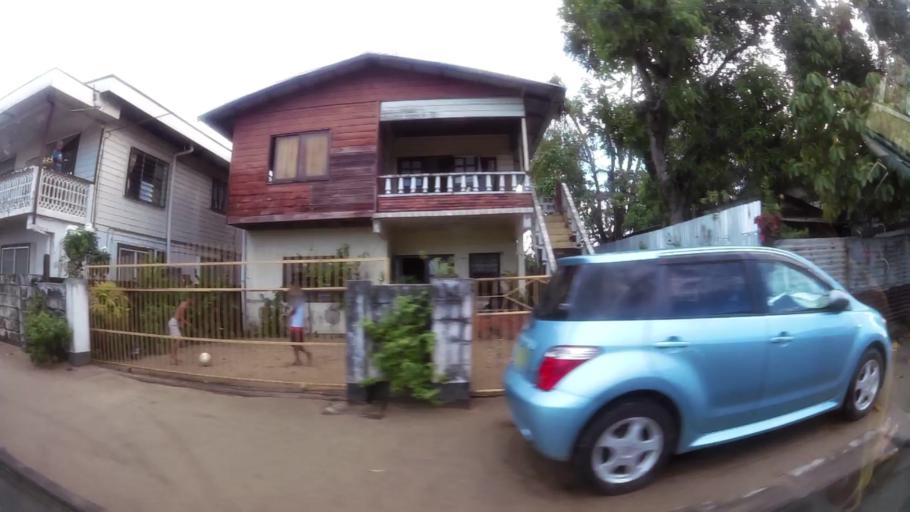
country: SR
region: Paramaribo
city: Paramaribo
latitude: 5.8224
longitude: -55.1784
